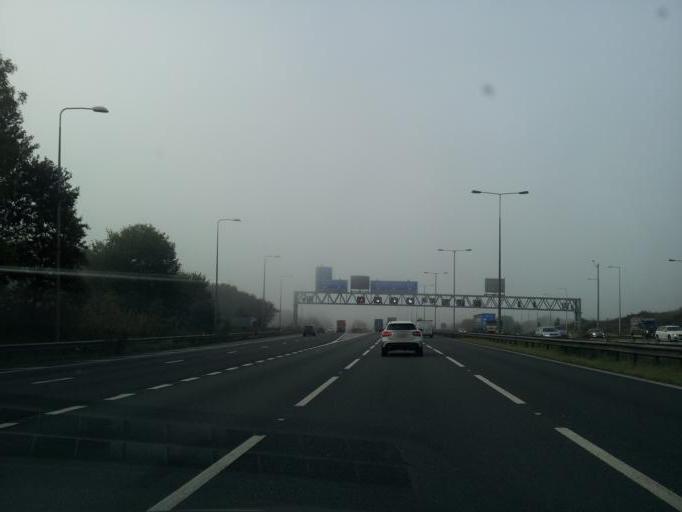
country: GB
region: England
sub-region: Kirklees
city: Cleckheaton
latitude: 53.7420
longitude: -1.7203
